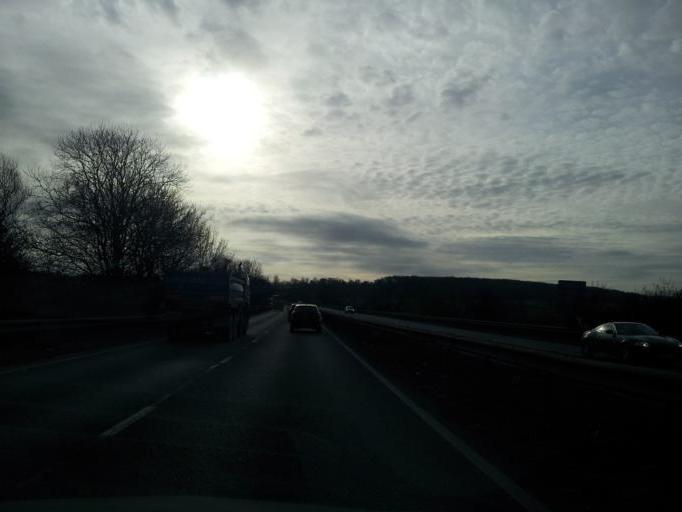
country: GB
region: England
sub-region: District of Rutland
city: Tinwell
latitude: 52.6419
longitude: -0.4987
